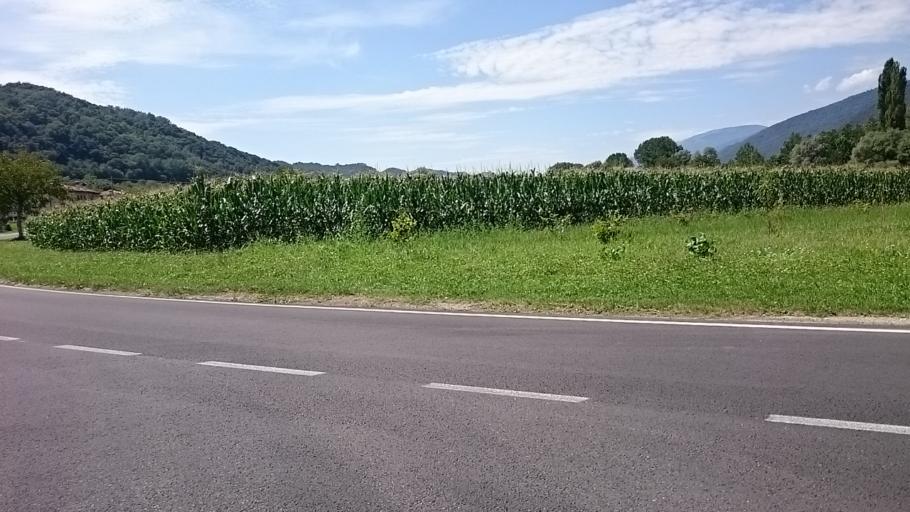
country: IT
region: Veneto
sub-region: Provincia di Treviso
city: Revine
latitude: 45.9929
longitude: 12.2469
